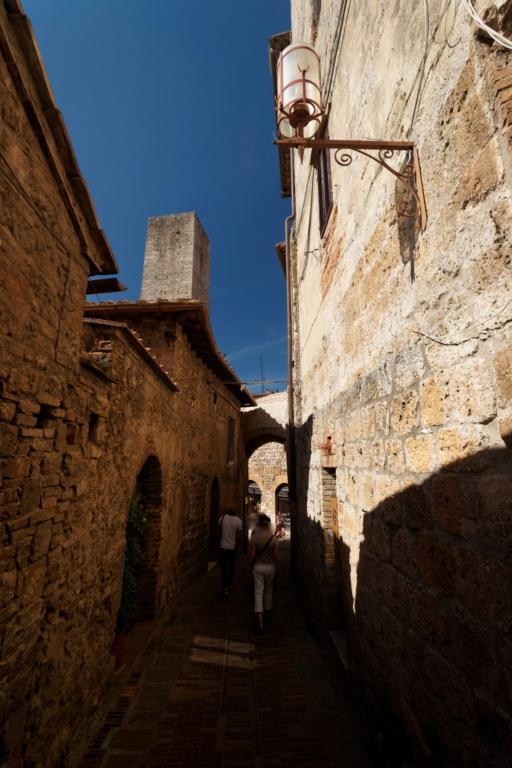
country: IT
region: Tuscany
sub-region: Provincia di Siena
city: San Gimignano
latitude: 43.4669
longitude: 11.0434
